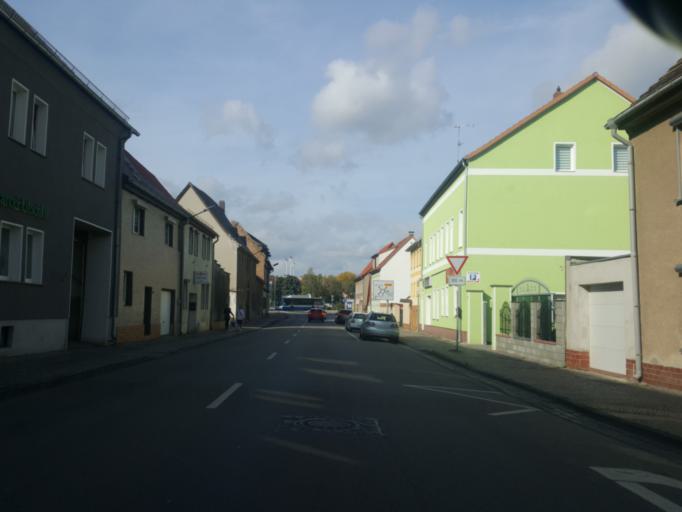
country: DE
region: Saxony-Anhalt
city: Volkstedt
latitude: 51.5334
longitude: 11.5467
